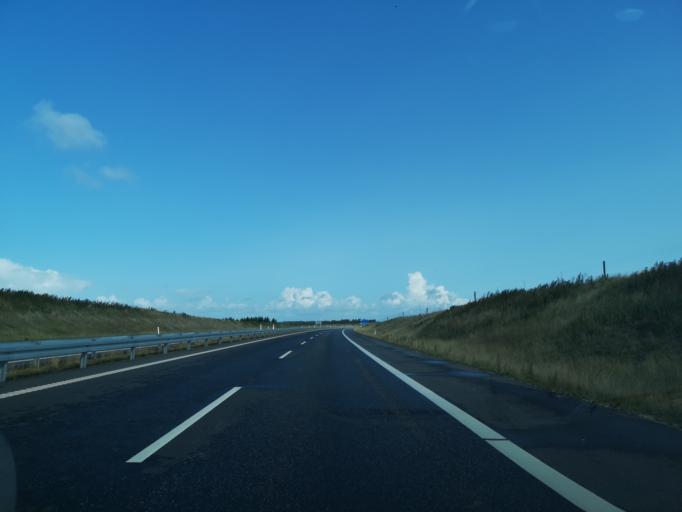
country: DK
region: Central Jutland
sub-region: Herning Kommune
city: Snejbjerg
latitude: 56.1372
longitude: 8.8697
